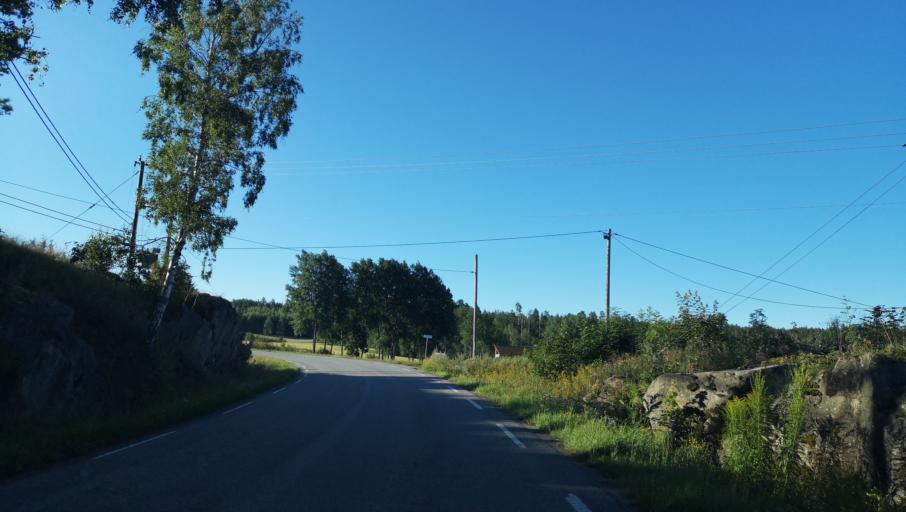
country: NO
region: Ostfold
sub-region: Hobol
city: Tomter
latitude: 59.6509
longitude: 11.0104
